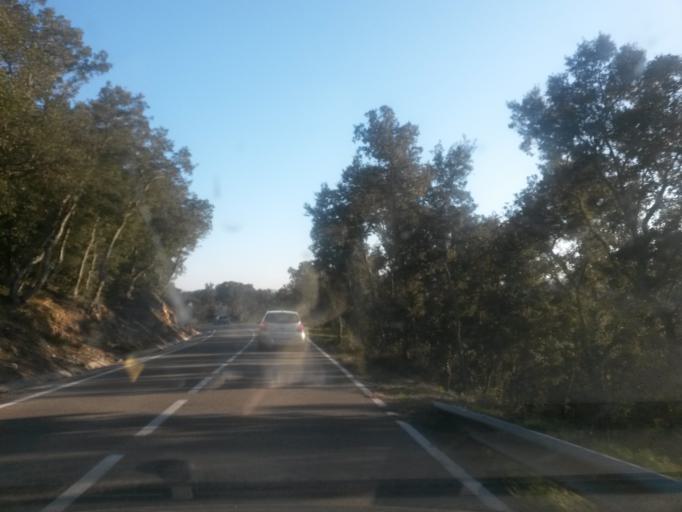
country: ES
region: Catalonia
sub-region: Provincia de Girona
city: Macanet de Cabrenys
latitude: 42.3850
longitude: 2.7864
